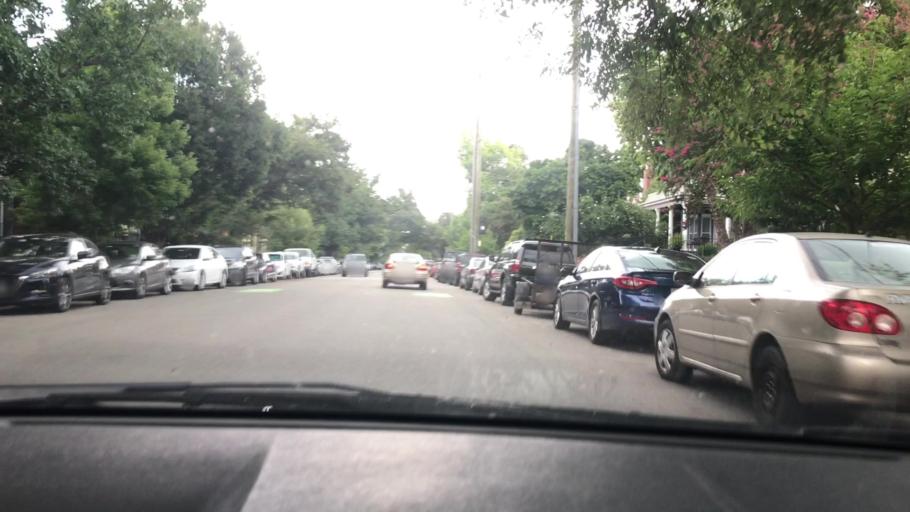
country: US
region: Virginia
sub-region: City of Richmond
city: Richmond
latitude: 37.5573
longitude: -77.4849
